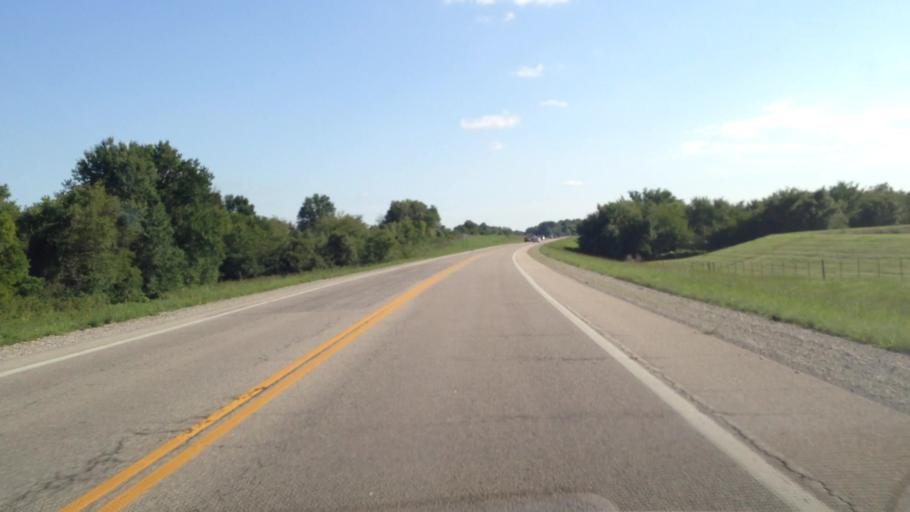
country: US
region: Kansas
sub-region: Crawford County
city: Arma
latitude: 37.5374
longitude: -94.7091
